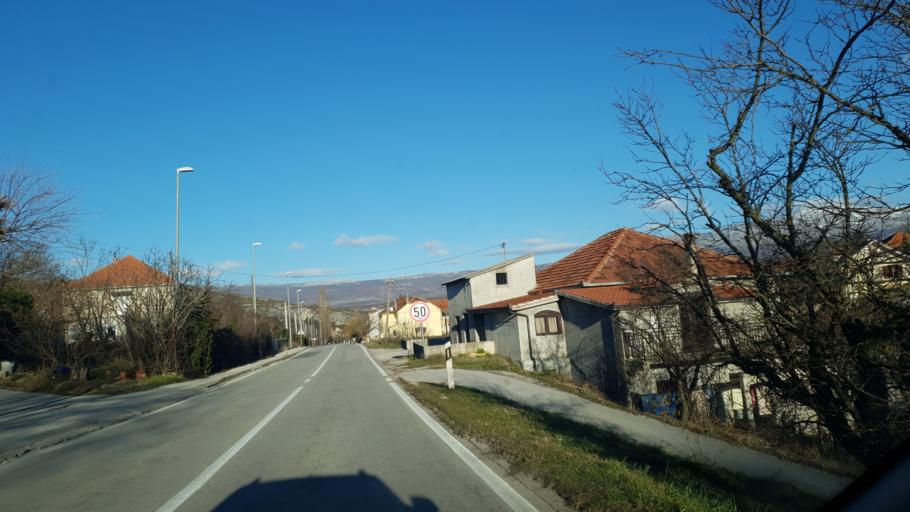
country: HR
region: Splitsko-Dalmatinska
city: Sinj
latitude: 43.7143
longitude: 16.6624
